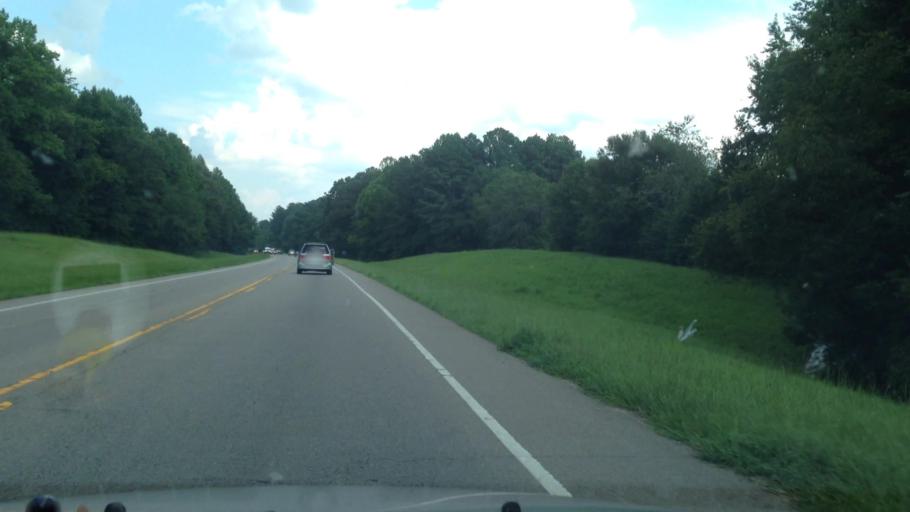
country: US
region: North Carolina
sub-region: Lee County
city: Broadway
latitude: 35.4403
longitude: -79.0956
